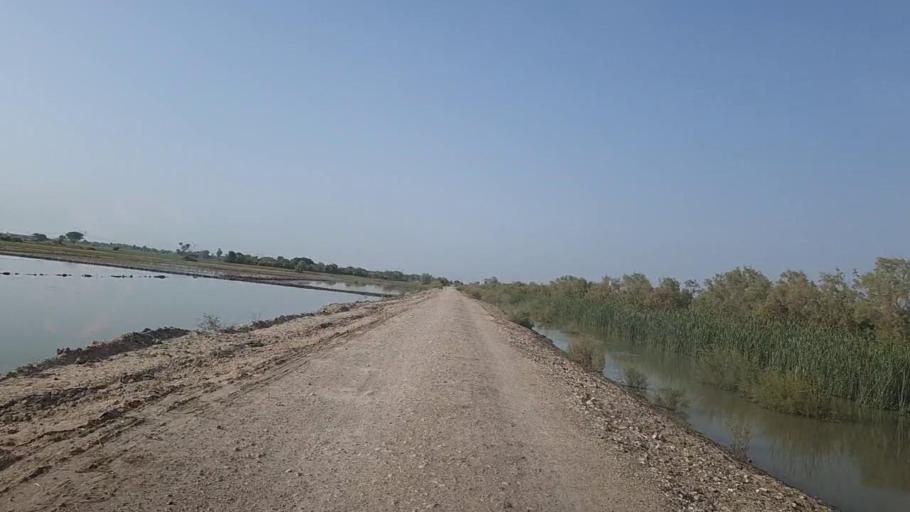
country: PK
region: Sindh
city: Sita Road
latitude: 27.0976
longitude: 67.8732
